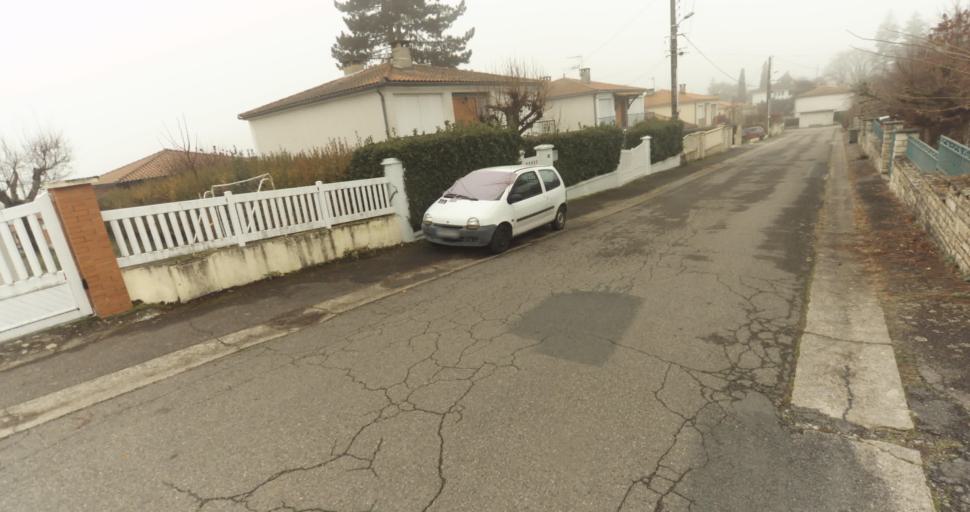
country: FR
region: Midi-Pyrenees
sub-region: Departement du Lot
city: Figeac
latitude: 44.6175
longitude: 2.0430
